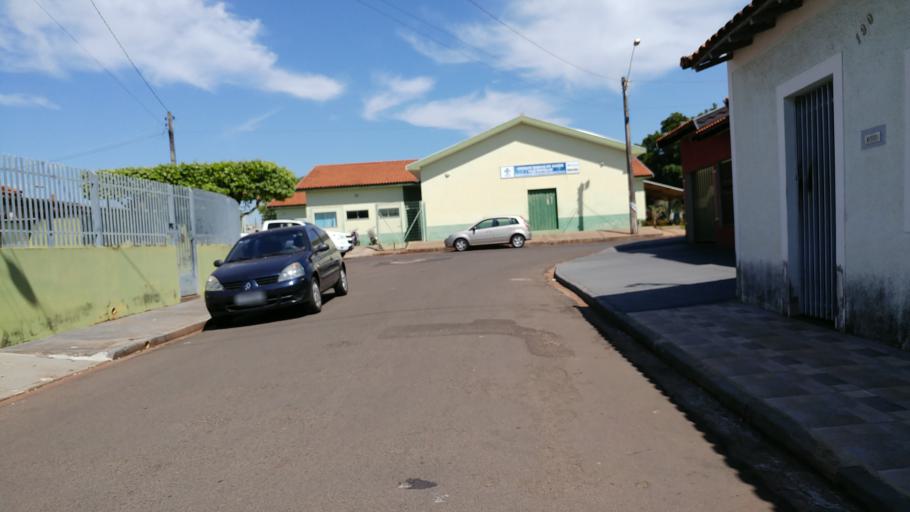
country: BR
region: Sao Paulo
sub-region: Paraguacu Paulista
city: Paraguacu Paulista
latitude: -22.4282
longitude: -50.5800
